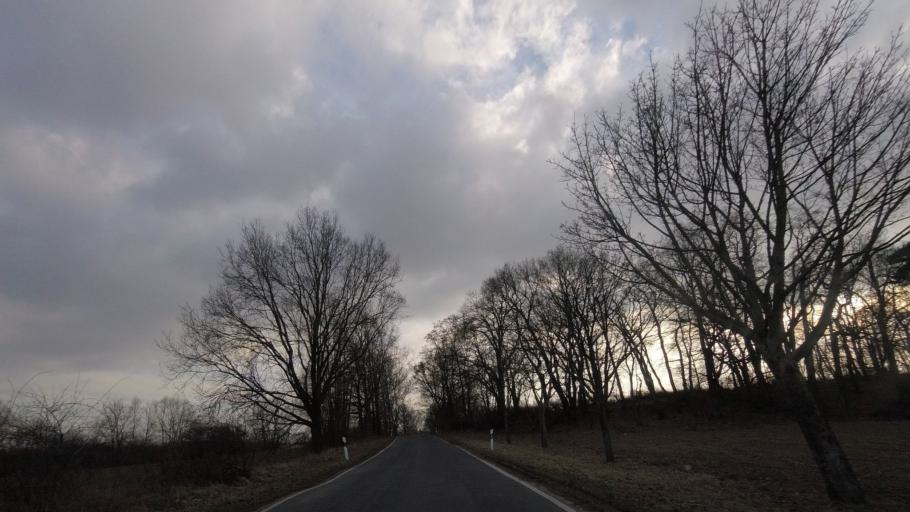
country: DE
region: Brandenburg
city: Wiesenburg
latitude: 52.1451
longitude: 12.5195
